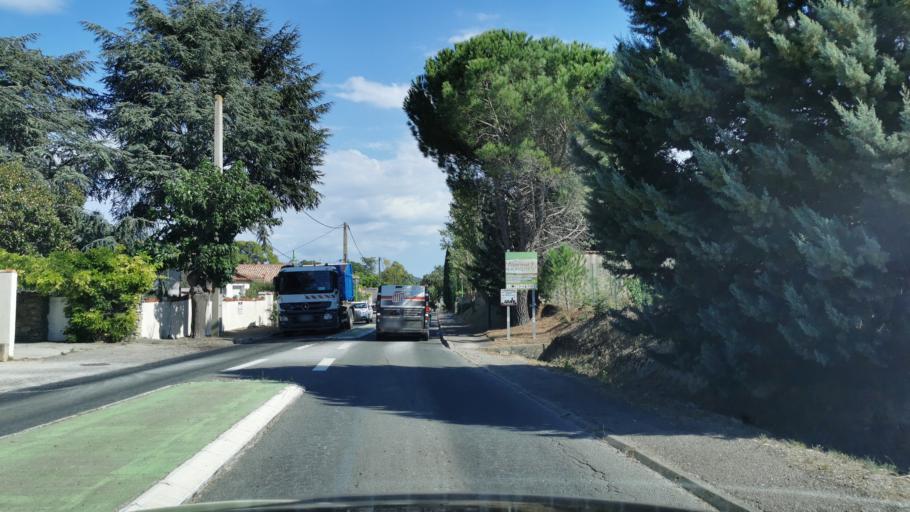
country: FR
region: Languedoc-Roussillon
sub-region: Departement de l'Aude
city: Azille
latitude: 43.2535
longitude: 2.6466
